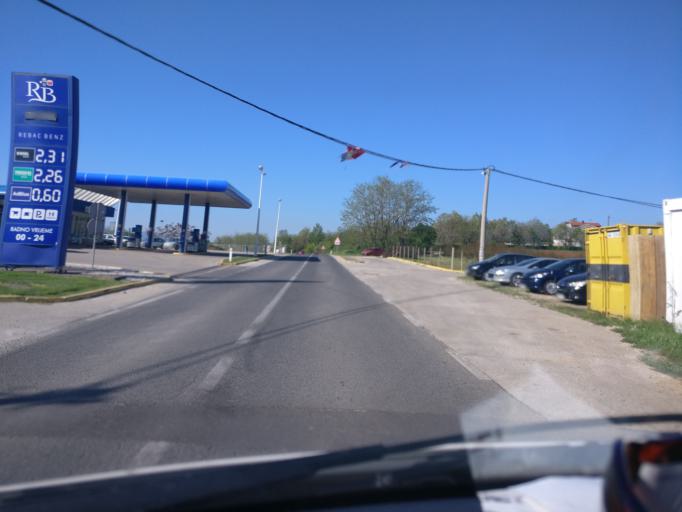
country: BA
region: Federation of Bosnia and Herzegovina
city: Tasovcici
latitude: 43.1344
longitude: 17.7742
